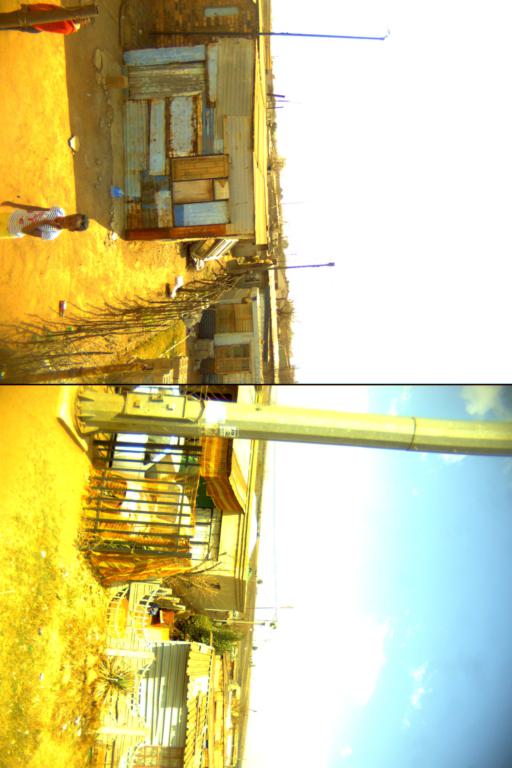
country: ZA
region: Mpumalanga
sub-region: Nkangala District Municipality
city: Delmas
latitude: -26.1049
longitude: 28.7046
